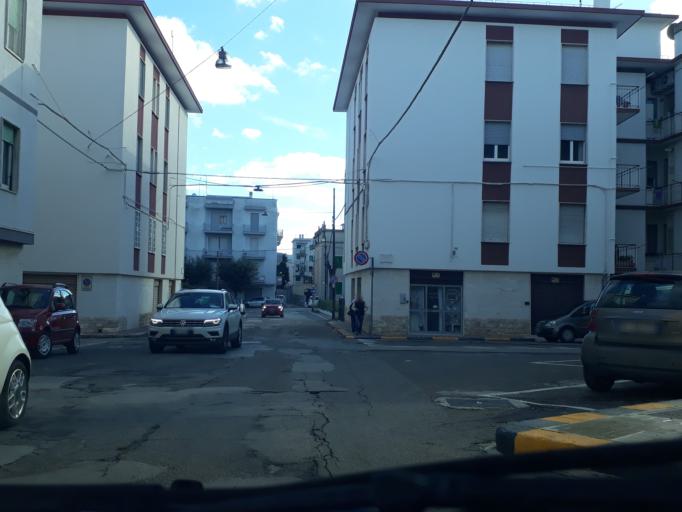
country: IT
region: Apulia
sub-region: Provincia di Brindisi
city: Fasano
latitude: 40.8326
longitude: 17.3552
